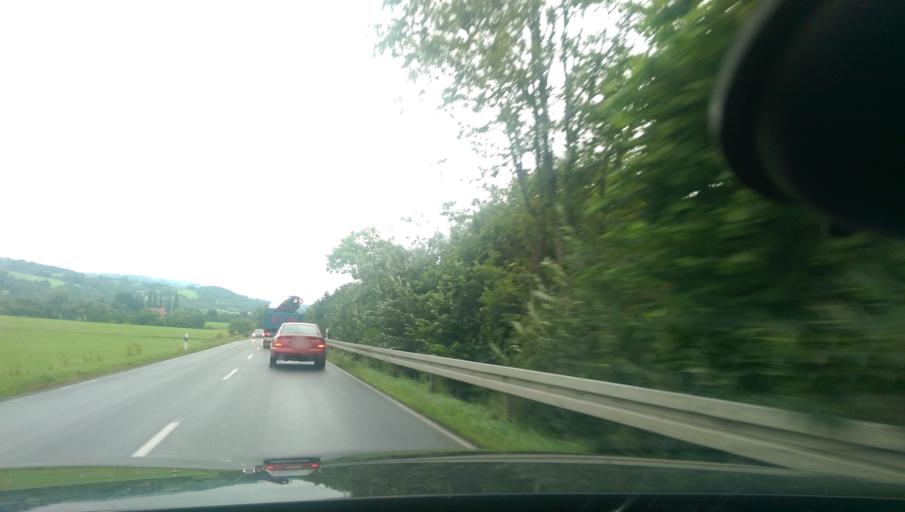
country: DE
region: Hesse
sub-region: Regierungsbezirk Kassel
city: Grossalmerode
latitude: 51.2216
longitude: 9.8050
